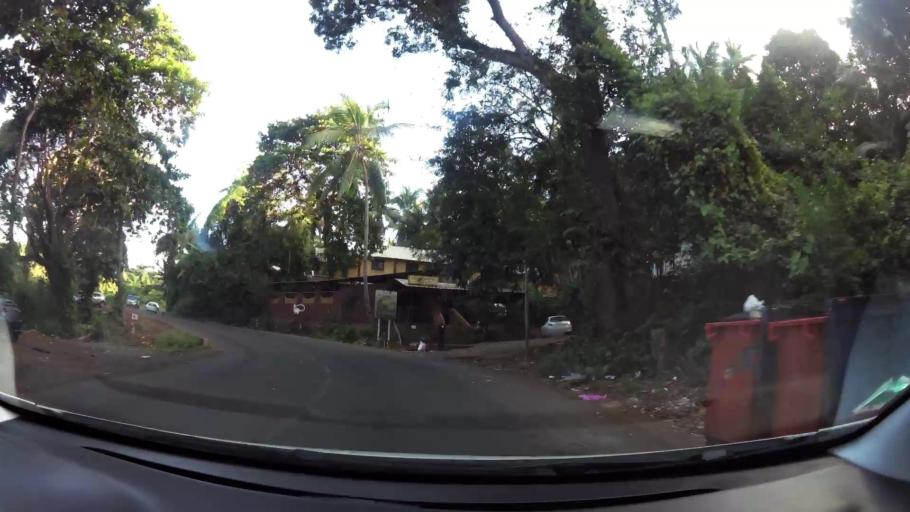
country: YT
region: Dembeni
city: Dembeni
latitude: -12.8184
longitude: 45.1966
